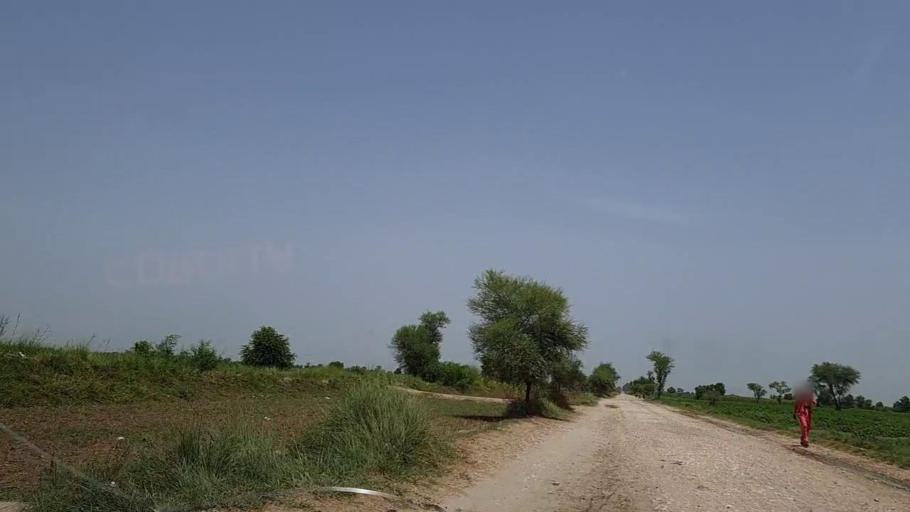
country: PK
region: Sindh
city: Tharu Shah
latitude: 26.9082
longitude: 68.0046
